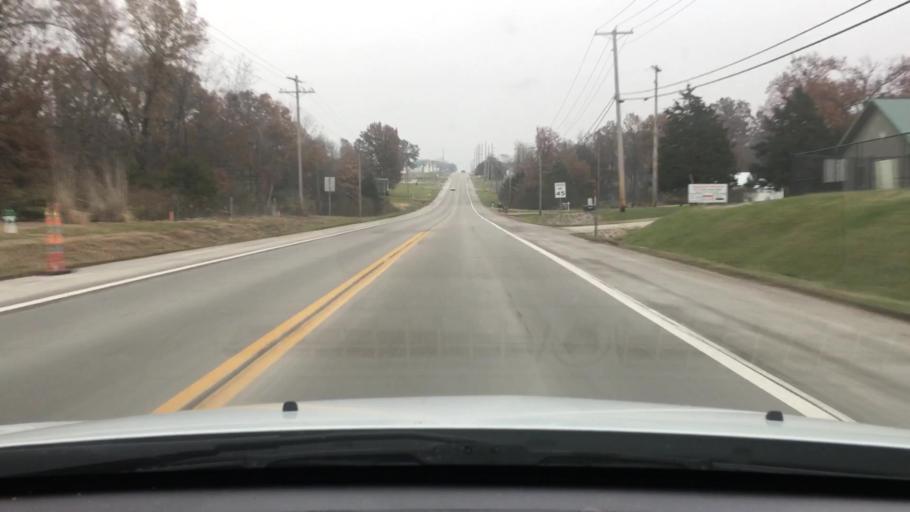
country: US
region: Missouri
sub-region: Audrain County
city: Mexico
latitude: 39.1634
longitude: -91.8378
